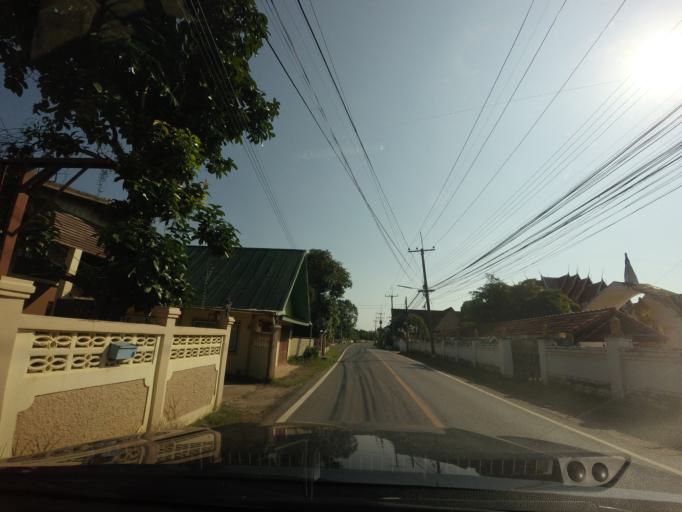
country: TH
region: Nan
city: Nan
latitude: 18.7770
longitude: 100.7847
